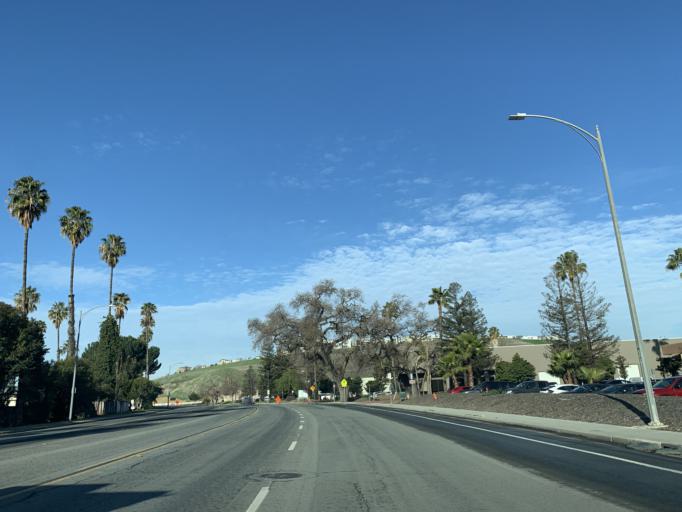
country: US
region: California
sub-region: Santa Clara County
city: Seven Trees
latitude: 37.2798
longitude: -121.8448
